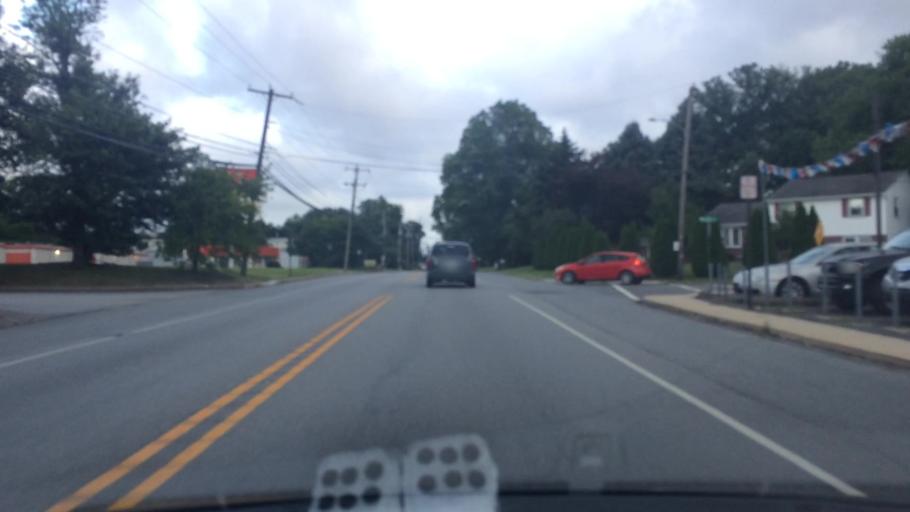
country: US
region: Pennsylvania
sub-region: Delaware County
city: Village Green-Green Ridge
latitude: 39.8505
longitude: -75.4263
